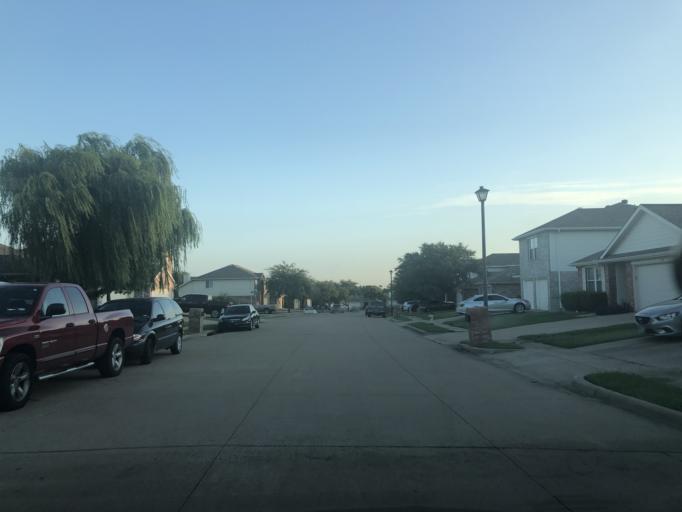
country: US
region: Texas
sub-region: Dallas County
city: Duncanville
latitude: 32.6537
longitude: -96.9714
